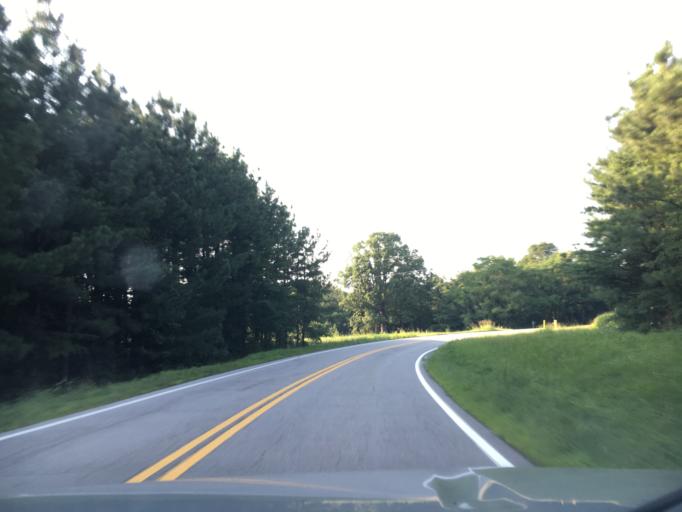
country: US
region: Virginia
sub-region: Pittsylvania County
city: Chatham
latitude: 36.8143
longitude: -79.2640
